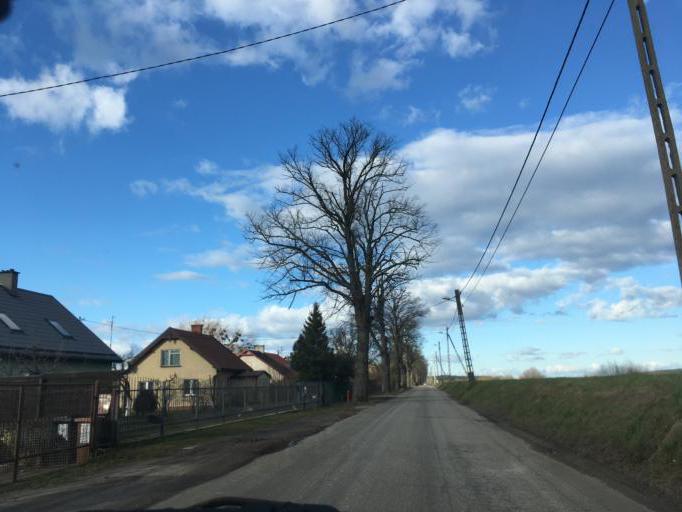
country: PL
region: Pomeranian Voivodeship
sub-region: Powiat nowodworski
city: Ostaszewo
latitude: 54.3200
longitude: 18.9314
